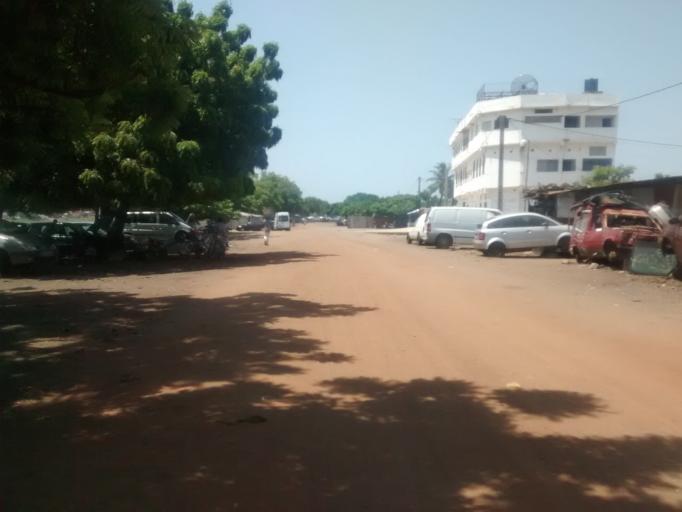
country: TG
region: Maritime
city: Lome
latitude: 6.1468
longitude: 1.2390
